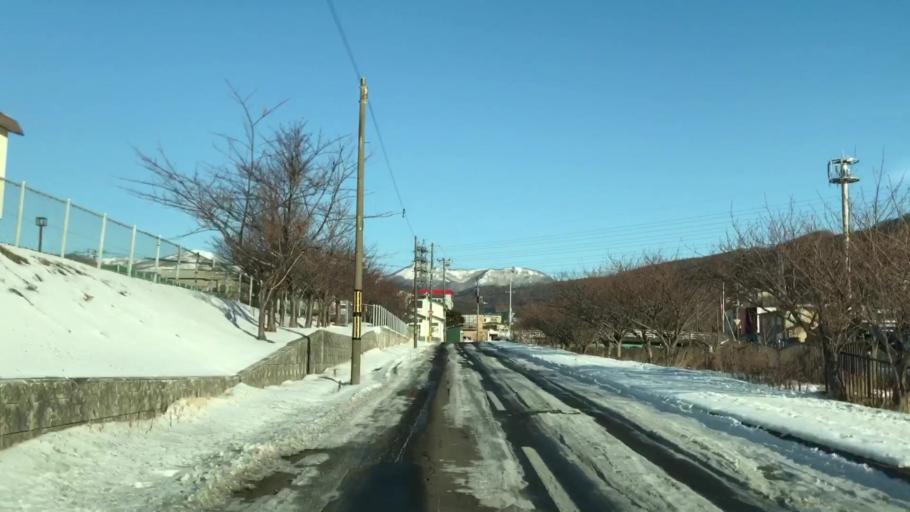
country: JP
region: Hokkaido
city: Muroran
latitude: 42.3695
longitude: 141.0377
